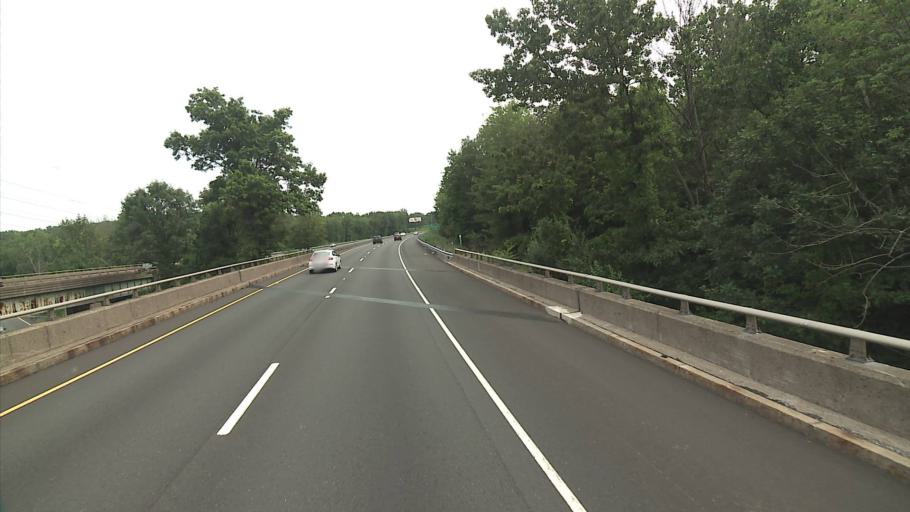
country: US
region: Connecticut
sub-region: New Haven County
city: Middlebury
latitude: 41.5355
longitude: -73.0868
